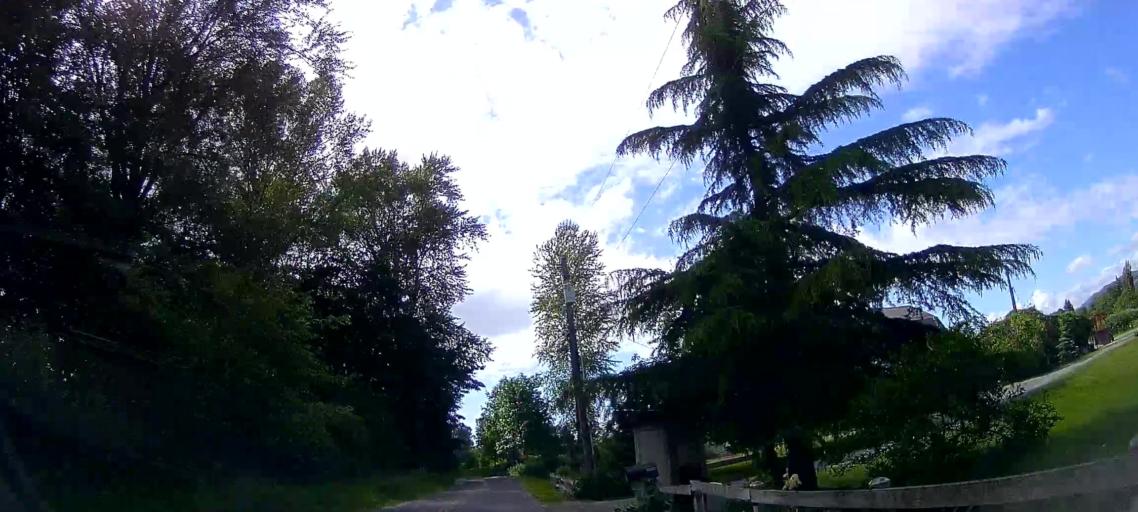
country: US
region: Washington
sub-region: Skagit County
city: Sedro-Woolley
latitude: 48.4898
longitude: -122.2288
